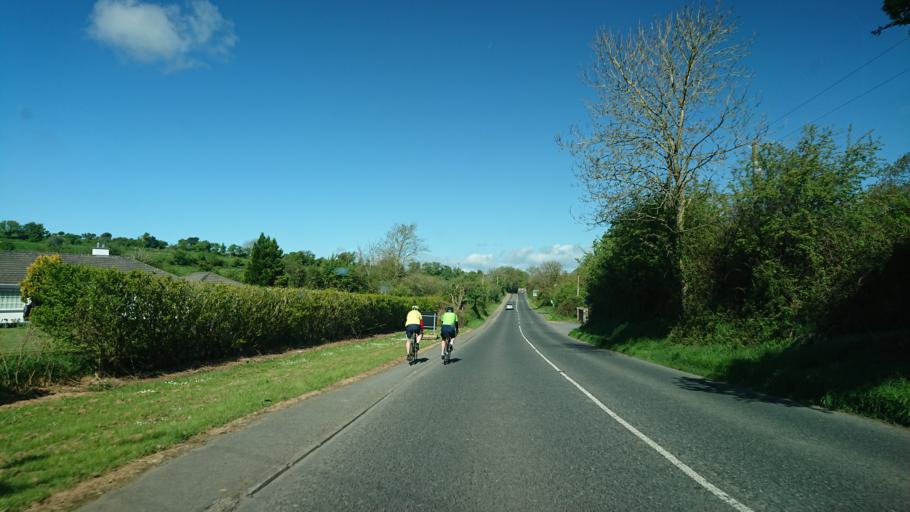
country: IE
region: Munster
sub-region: Waterford
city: Waterford
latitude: 52.2333
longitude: -7.0491
